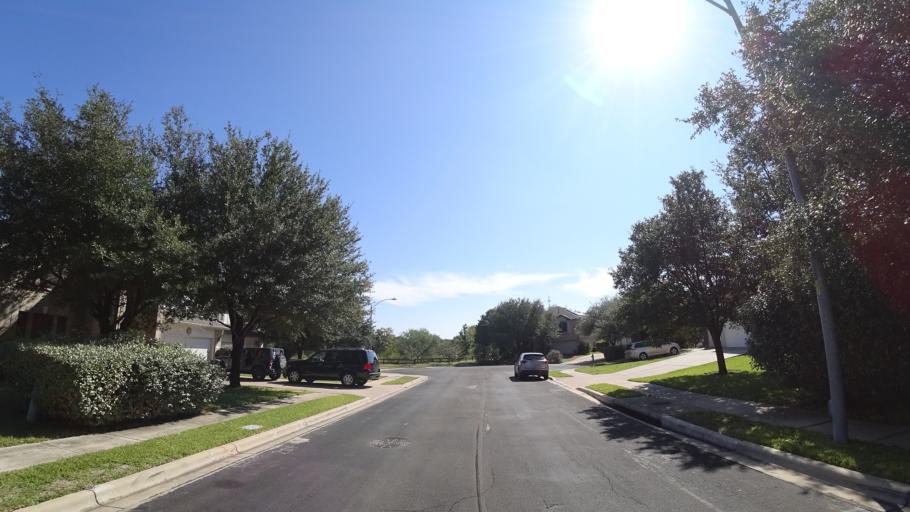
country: US
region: Texas
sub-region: Travis County
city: Shady Hollow
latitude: 30.1957
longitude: -97.8605
